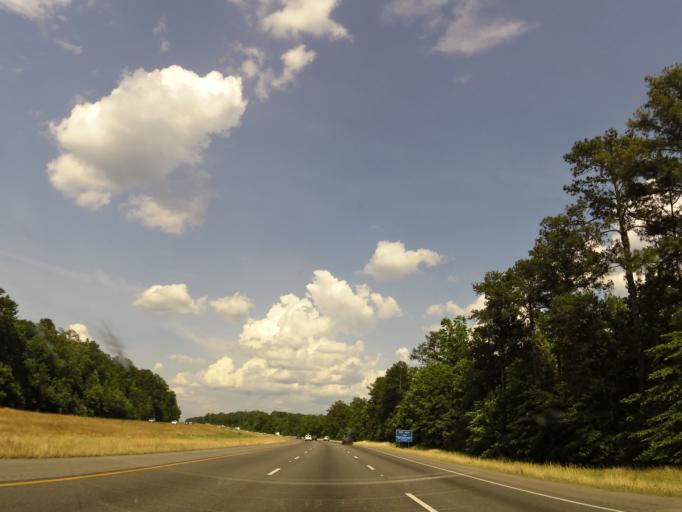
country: US
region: Alabama
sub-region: Tuscaloosa County
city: Coaling
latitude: 33.1835
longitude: -87.3463
